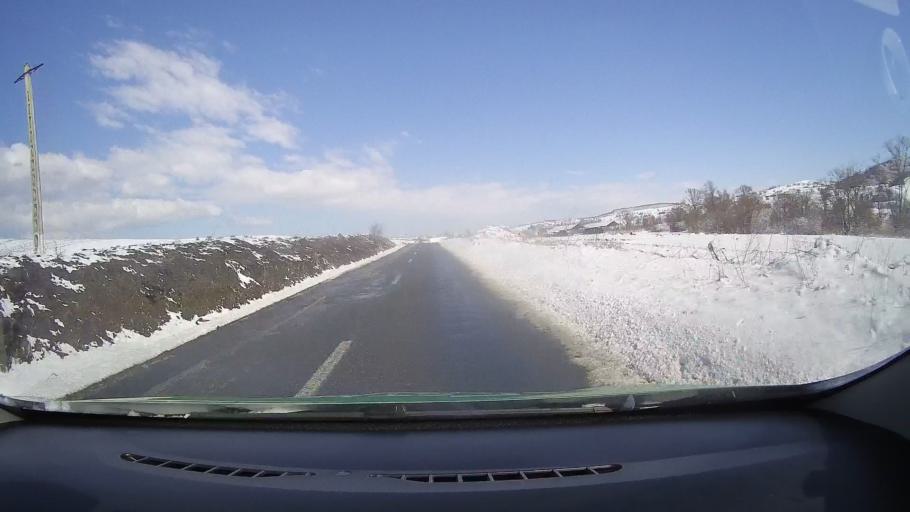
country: RO
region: Sibiu
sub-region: Comuna Vurpar
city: Vurpar
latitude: 45.8818
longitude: 24.3268
